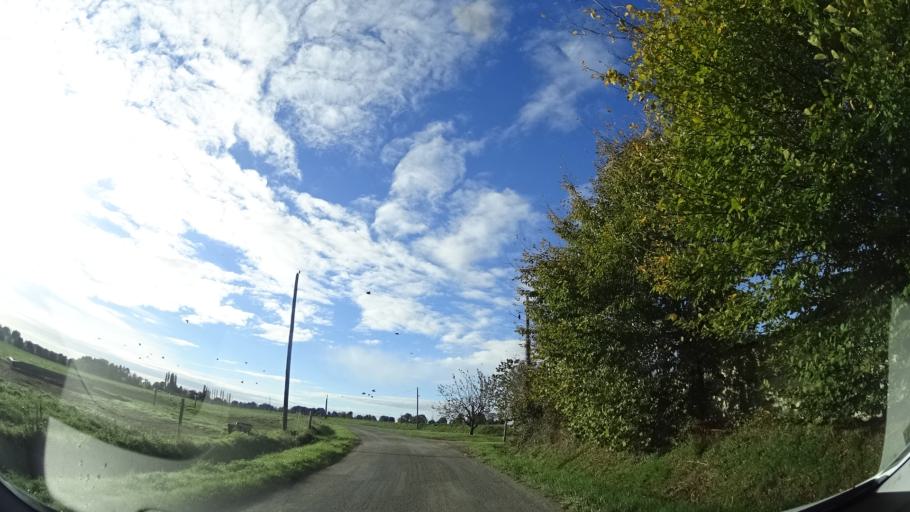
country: FR
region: Brittany
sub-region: Departement d'Ille-et-Vilaine
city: Geveze
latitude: 48.1976
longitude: -1.8199
